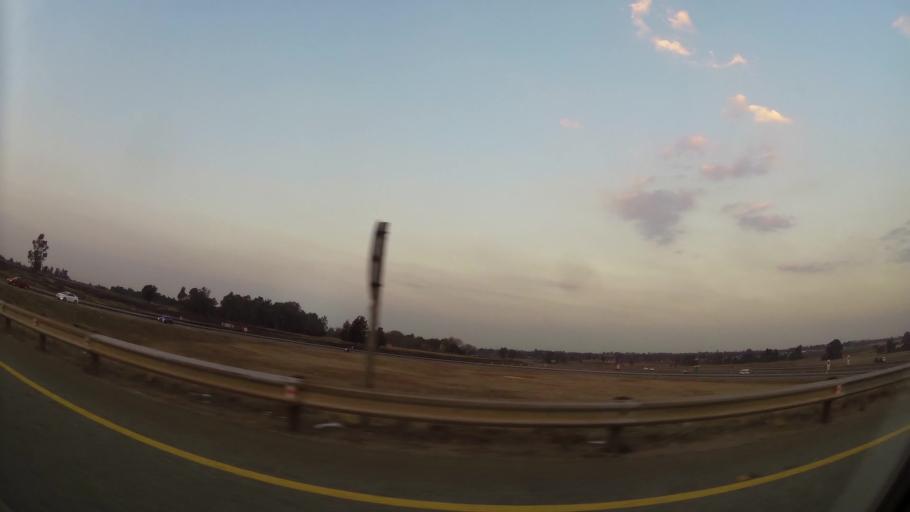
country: ZA
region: Gauteng
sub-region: Ekurhuleni Metropolitan Municipality
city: Springs
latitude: -26.2836
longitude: 28.4296
